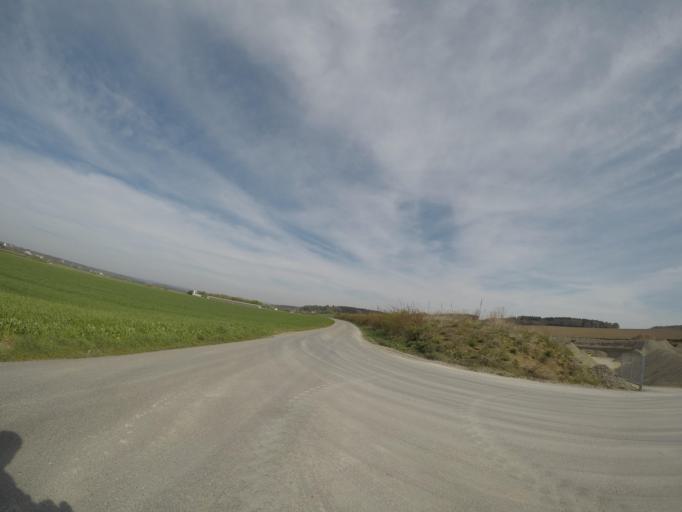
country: DE
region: Baden-Wuerttemberg
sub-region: Tuebingen Region
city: Boms
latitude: 48.0080
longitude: 9.5422
